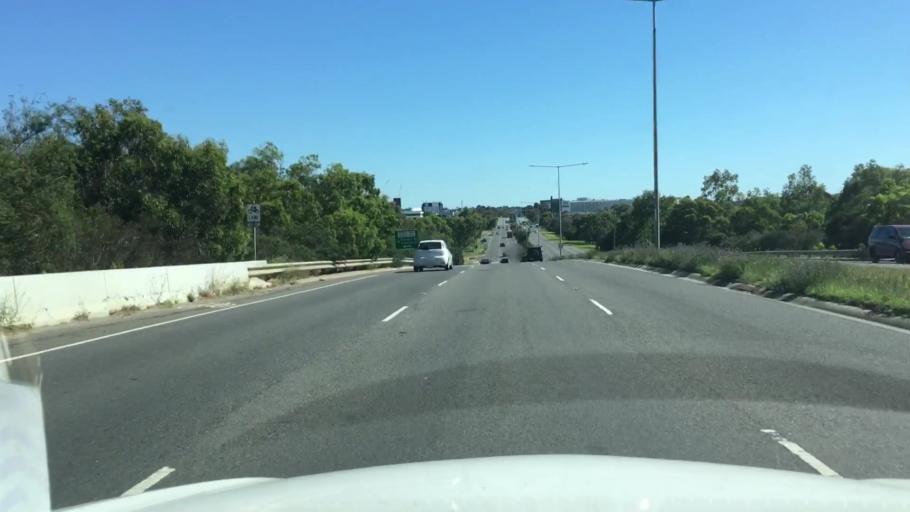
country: AU
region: Victoria
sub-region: Greater Dandenong
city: Springvale
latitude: -37.9387
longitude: 145.1402
